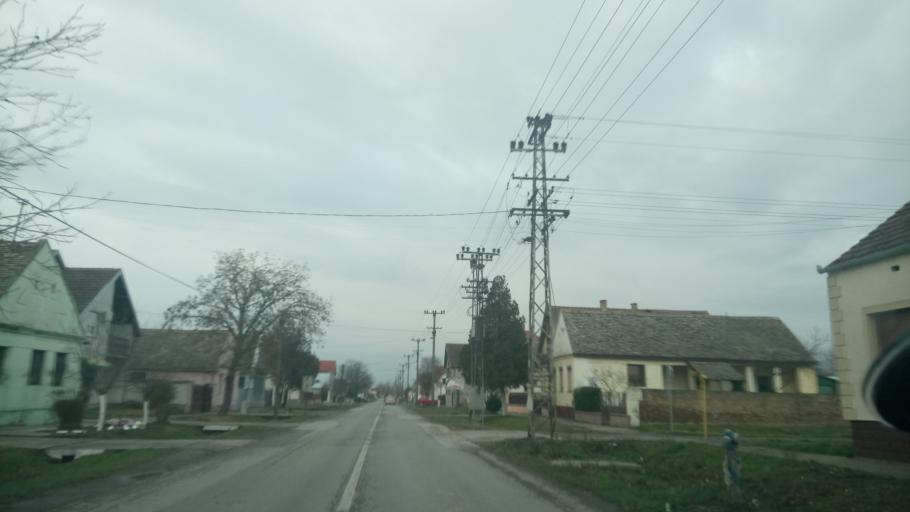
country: RS
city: Vojka
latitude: 44.9414
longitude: 20.1529
